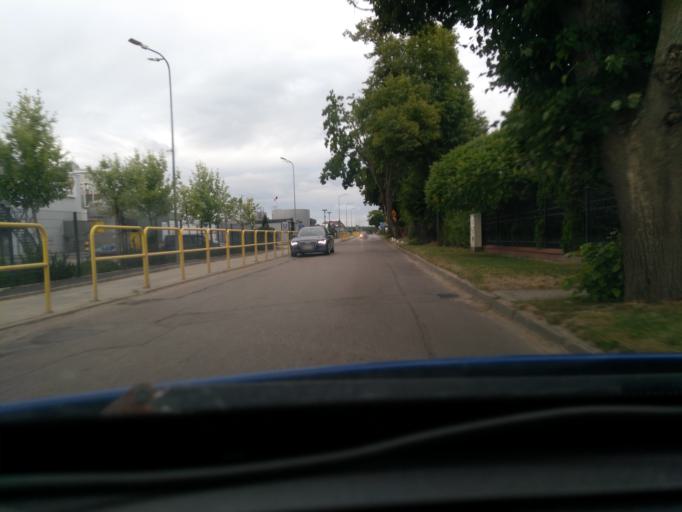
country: PL
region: Pomeranian Voivodeship
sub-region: Powiat kartuski
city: Banino
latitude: 54.3876
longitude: 18.4060
